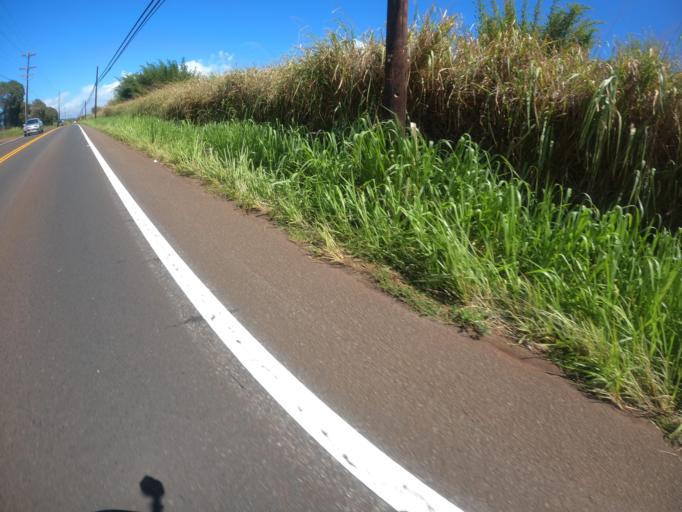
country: US
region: Hawaii
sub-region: Honolulu County
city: Schofield Barracks
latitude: 21.4604
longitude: -158.0570
